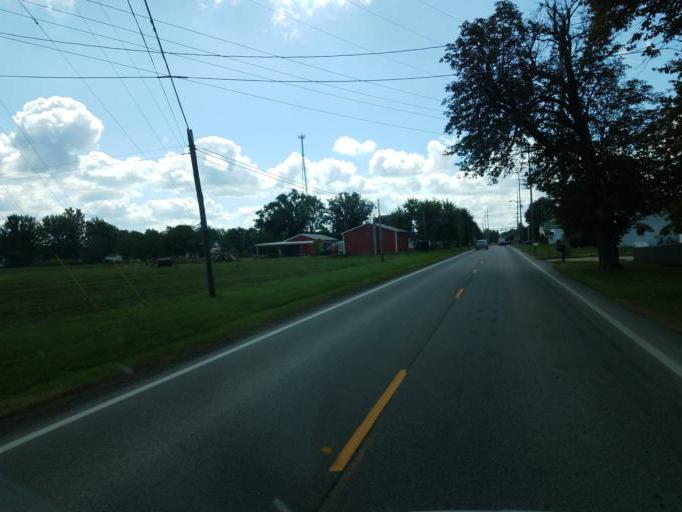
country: US
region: Ohio
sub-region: Wayne County
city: West Salem
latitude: 41.0292
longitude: -82.1262
